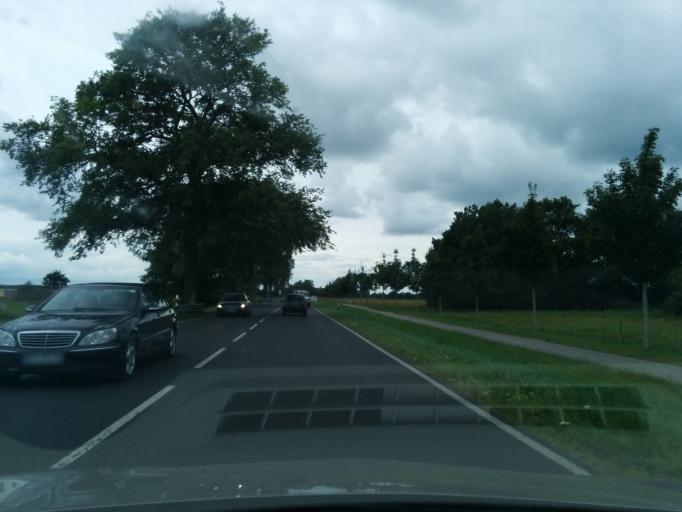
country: DE
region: Mecklenburg-Vorpommern
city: Ostseebad Zinnowitz
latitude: 54.0702
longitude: 13.8816
